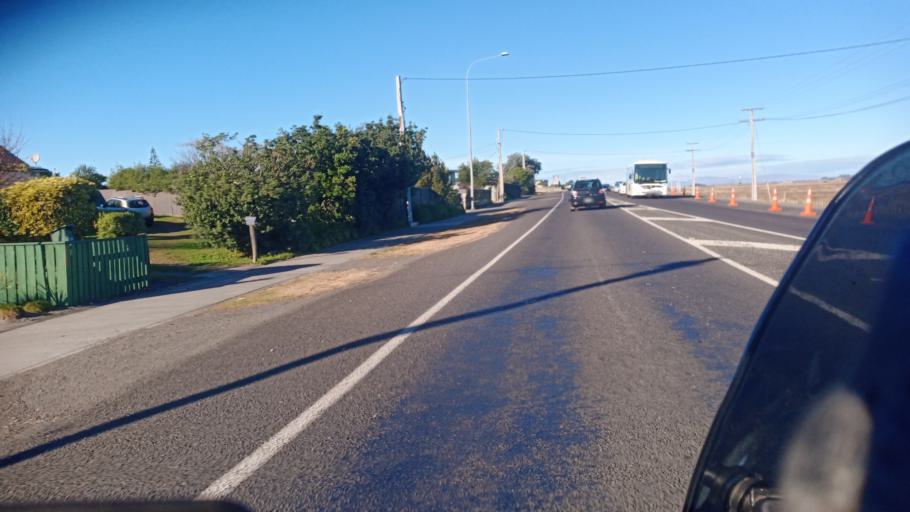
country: NZ
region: Hawke's Bay
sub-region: Napier City
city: Napier
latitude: -39.4396
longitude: 176.8706
